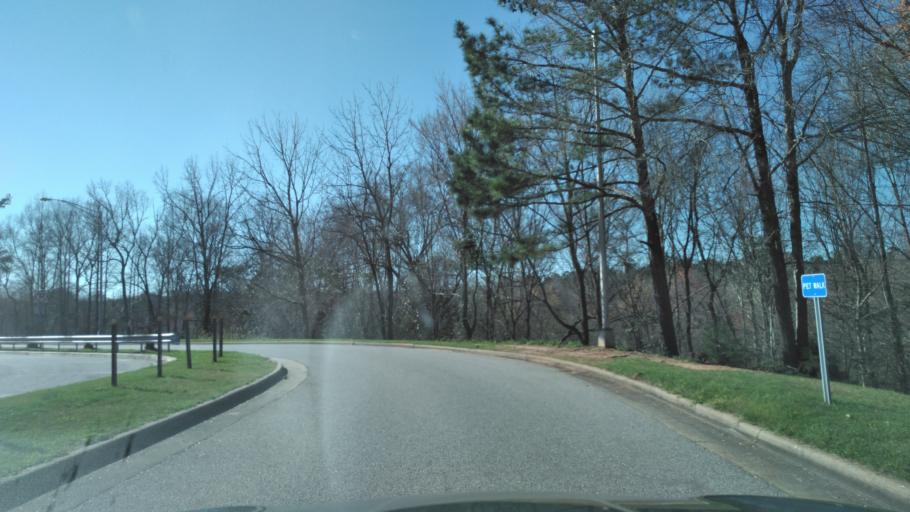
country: US
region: Alabama
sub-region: Butler County
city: Greenville
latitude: 31.8852
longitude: -86.6108
